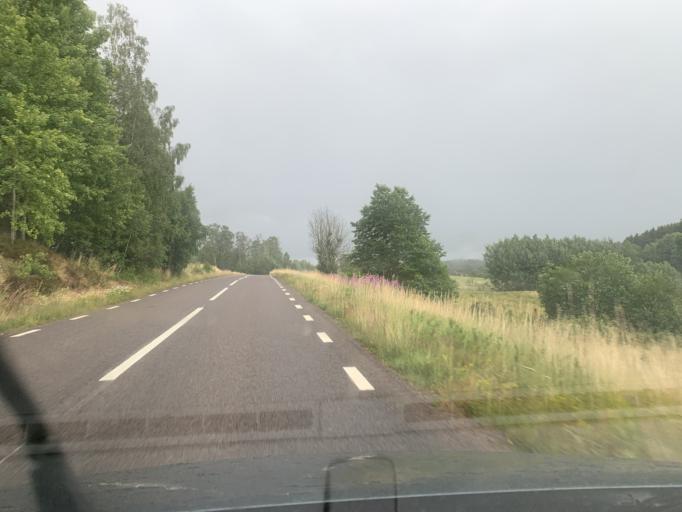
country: SE
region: Kalmar
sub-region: Vasterviks Kommun
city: Overum
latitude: 58.0011
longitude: 16.1767
